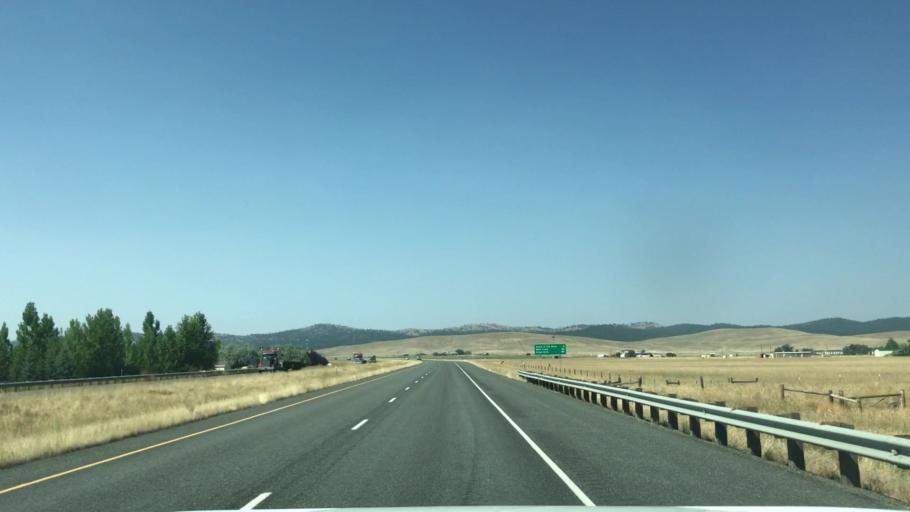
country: US
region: Montana
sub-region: Lewis and Clark County
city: Helena Valley Northwest
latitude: 46.7147
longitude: -112.0120
